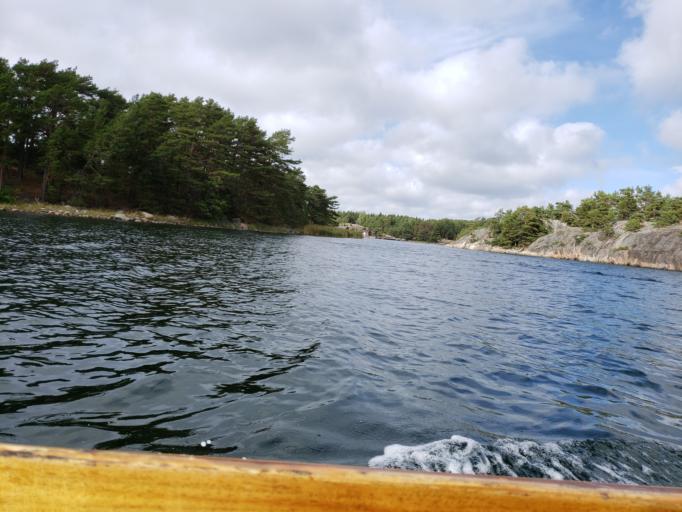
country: FI
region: Varsinais-Suomi
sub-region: Aboland-Turunmaa
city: Dragsfjaerd
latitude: 59.9036
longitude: 22.3589
